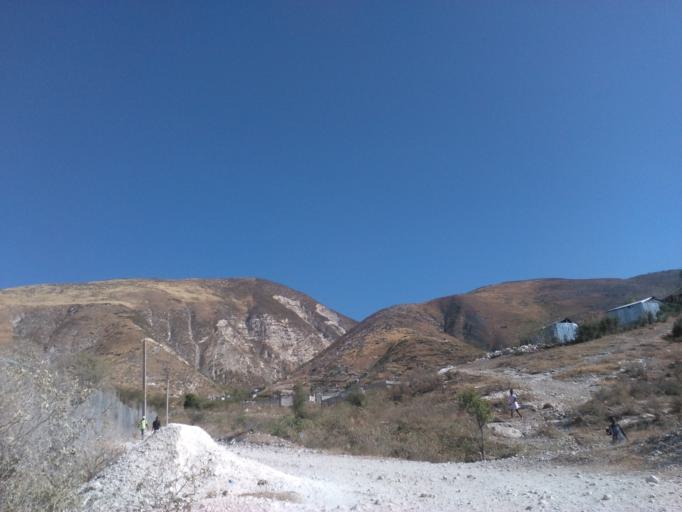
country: HT
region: Ouest
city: Croix des Bouquets
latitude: 18.6695
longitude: -72.2287
